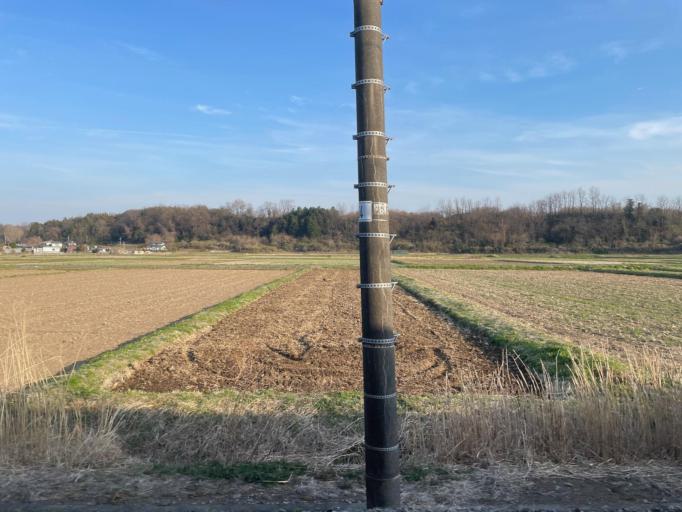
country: JP
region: Gunma
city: Annaka
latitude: 36.3100
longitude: 138.8792
